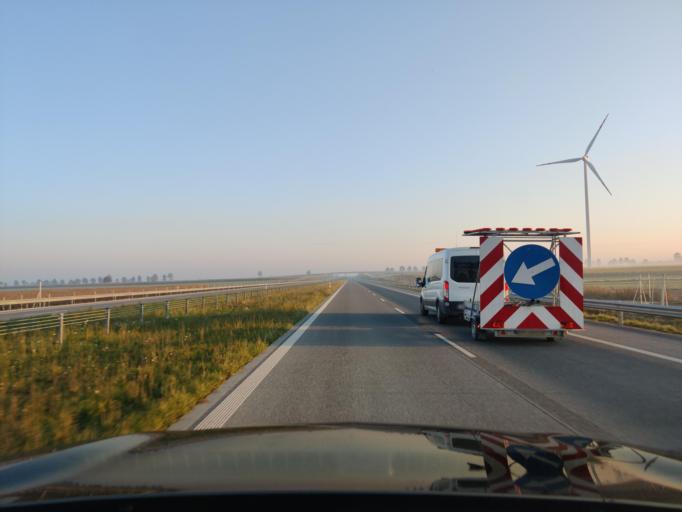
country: PL
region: Masovian Voivodeship
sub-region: Powiat mlawski
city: Wisniewo
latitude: 53.0529
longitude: 20.3624
